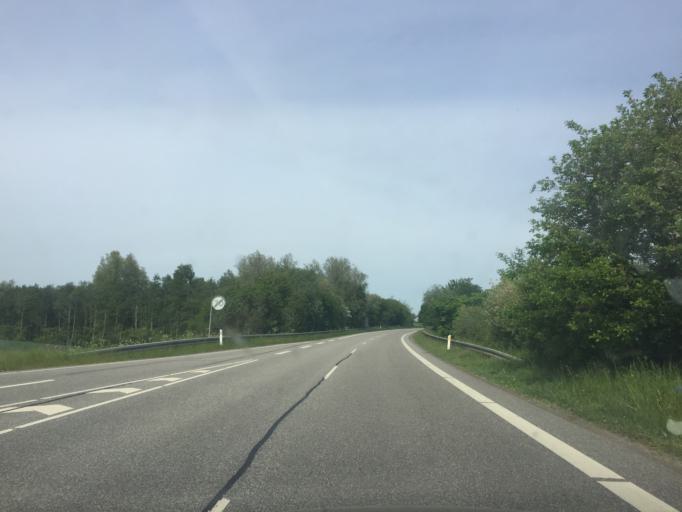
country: DK
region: South Denmark
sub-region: Nyborg Kommune
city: Nyborg
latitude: 55.3138
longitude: 10.7285
